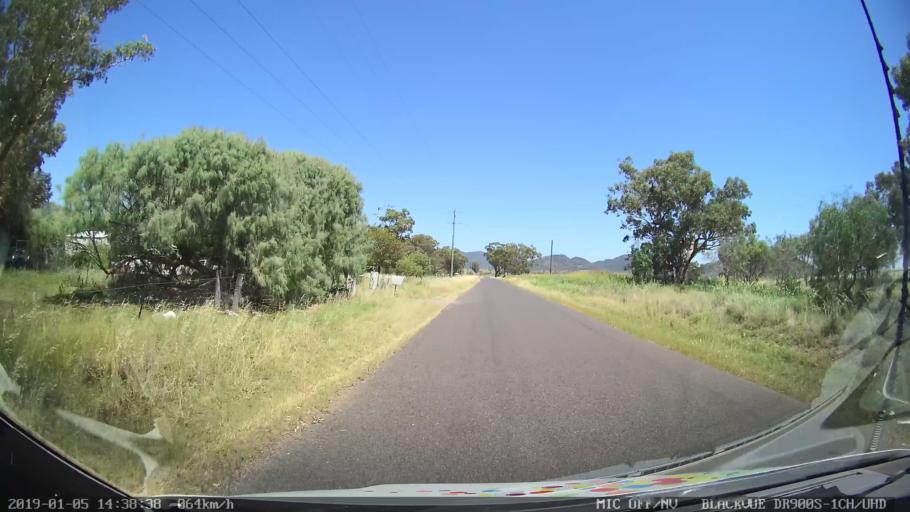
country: AU
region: New South Wales
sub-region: Tamworth Municipality
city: Phillip
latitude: -31.2501
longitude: 150.6929
